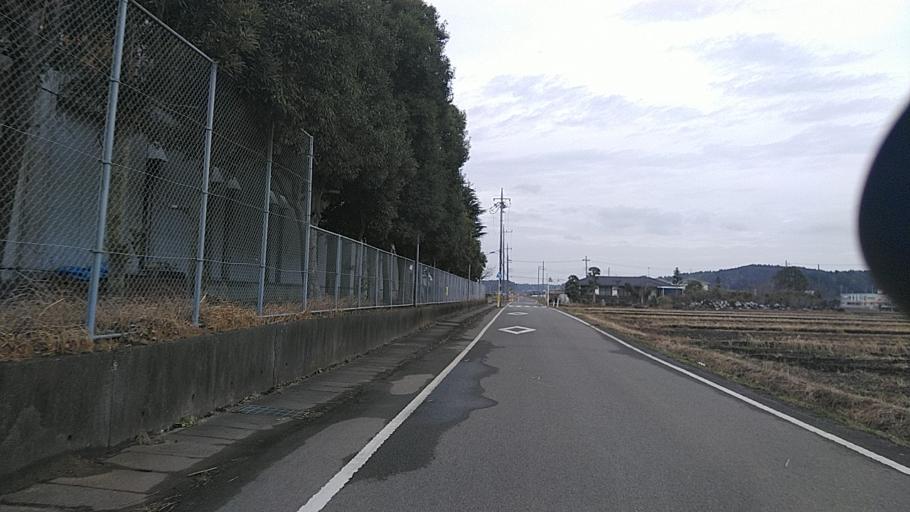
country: JP
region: Chiba
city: Togane
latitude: 35.5515
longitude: 140.3463
